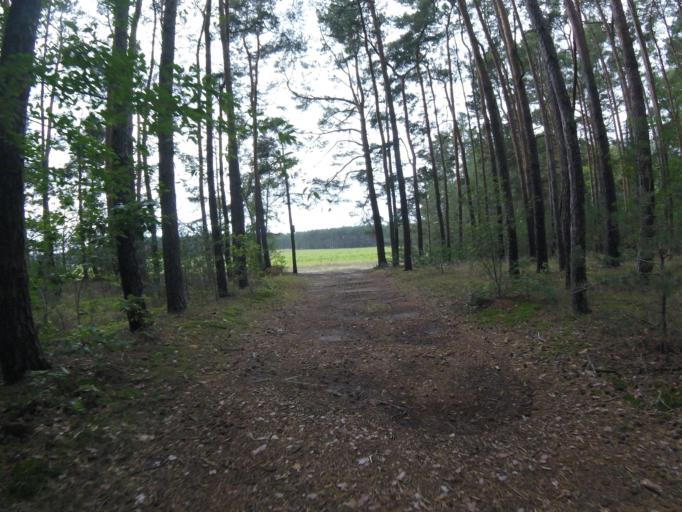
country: DE
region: Brandenburg
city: Bestensee
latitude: 52.2219
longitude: 13.6706
